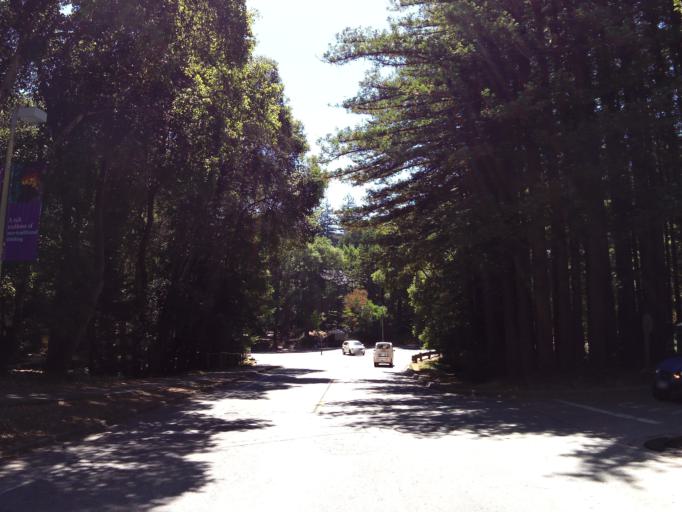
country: US
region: California
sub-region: Santa Cruz County
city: Pasatiempo
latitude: 36.9996
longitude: -122.0637
